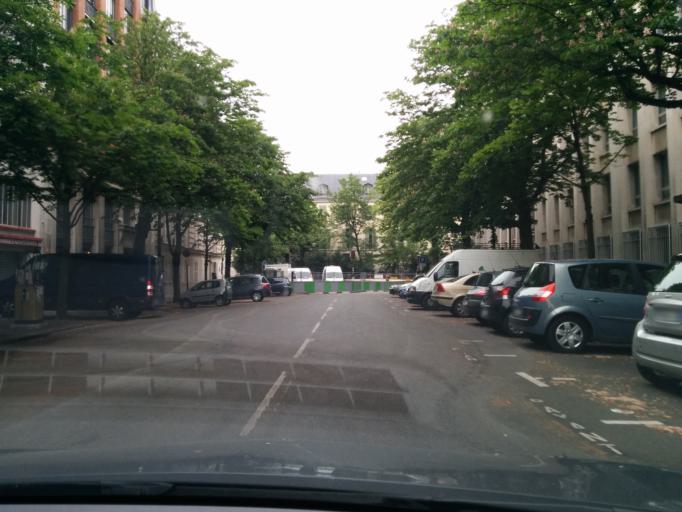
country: FR
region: Ile-de-France
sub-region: Paris
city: Paris
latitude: 48.8501
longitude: 2.3620
